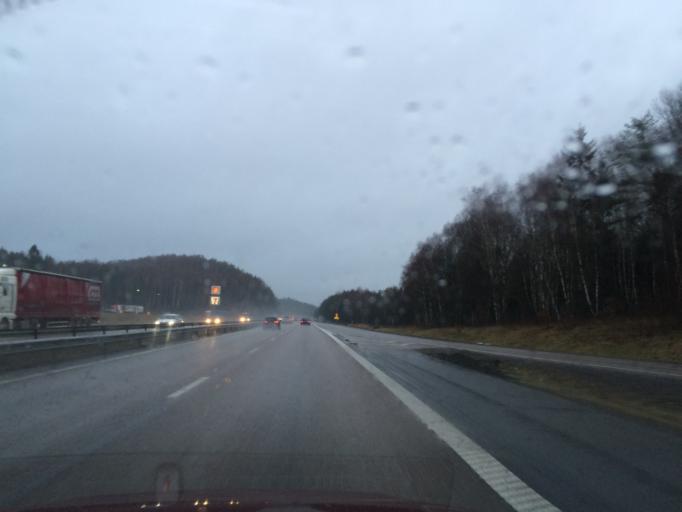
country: SE
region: Vaestra Goetaland
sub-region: Molndal
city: Lindome
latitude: 57.5532
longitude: 12.0533
